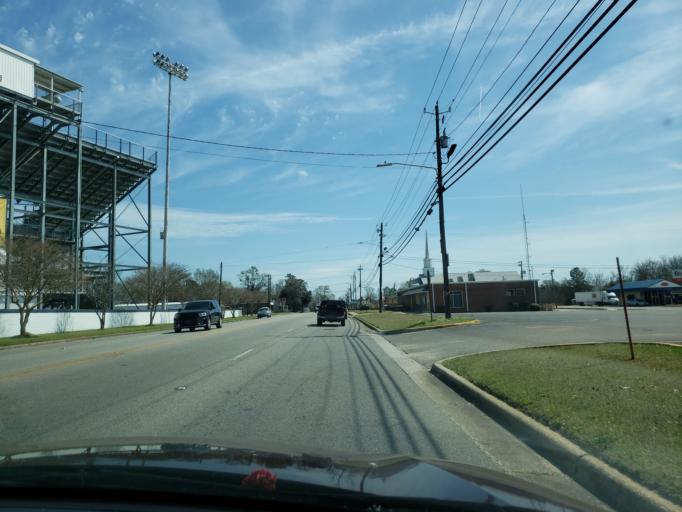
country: US
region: Alabama
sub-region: Elmore County
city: Tallassee
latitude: 32.5421
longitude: -85.9029
